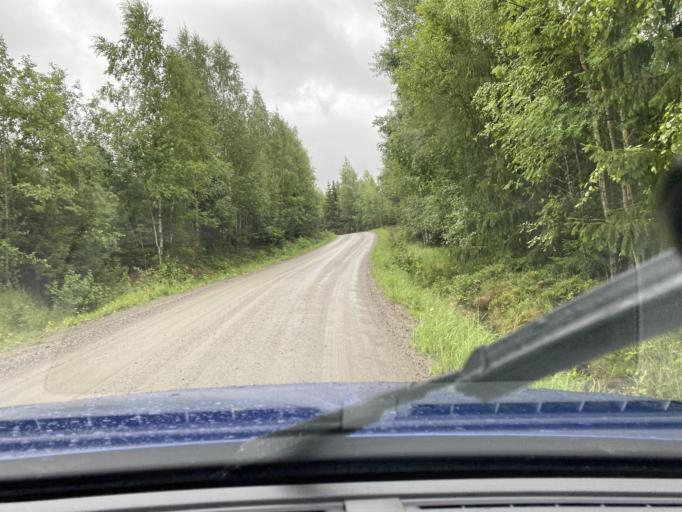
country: FI
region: Pirkanmaa
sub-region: Lounais-Pirkanmaa
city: Punkalaidun
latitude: 61.1470
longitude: 23.2640
